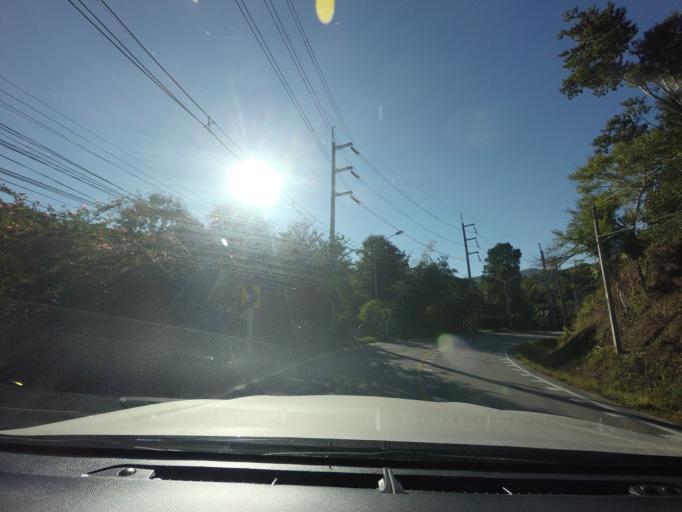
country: TH
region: Mae Hong Son
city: Mae Hi
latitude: 19.2040
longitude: 98.6725
